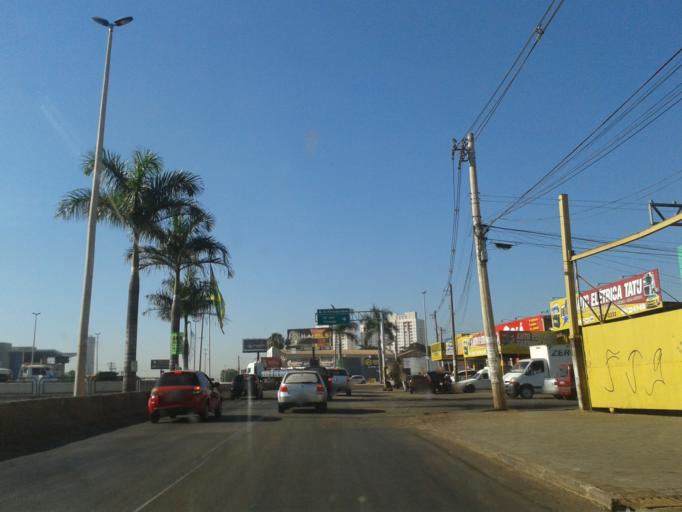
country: BR
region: Goias
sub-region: Goiania
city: Goiania
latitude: -16.6535
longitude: -49.3321
